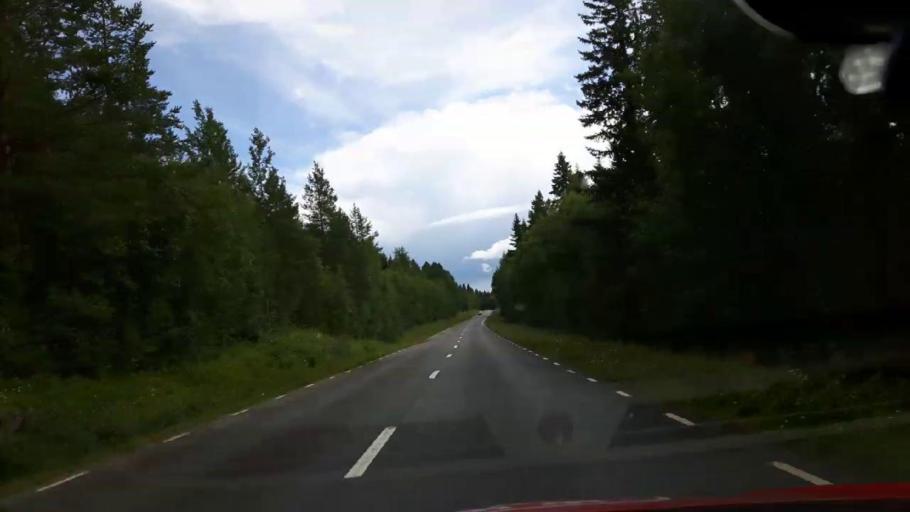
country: SE
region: Jaemtland
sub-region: Stroemsunds Kommun
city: Stroemsund
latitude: 64.3414
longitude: 14.9482
